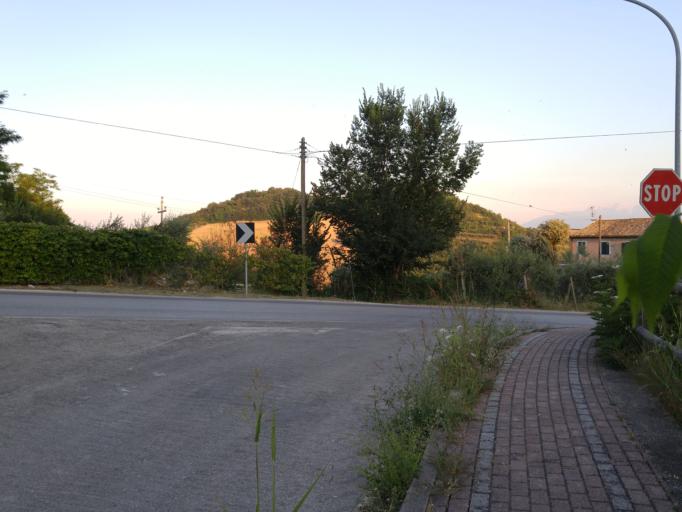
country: IT
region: Abruzzo
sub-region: Provincia di Teramo
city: Castilenti
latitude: 42.5365
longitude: 13.9207
